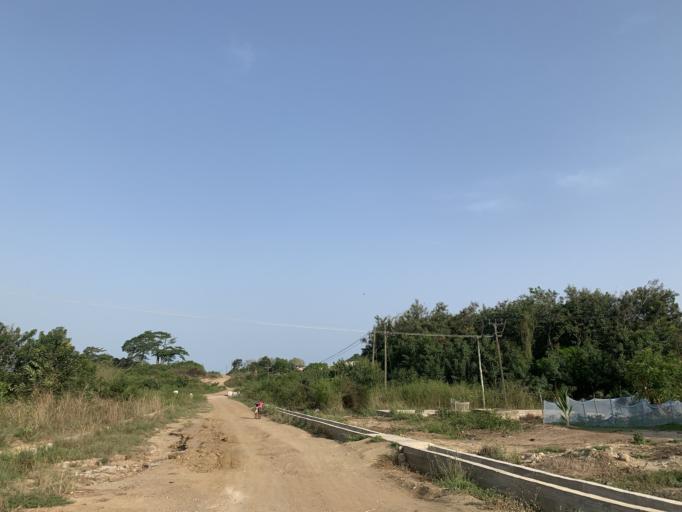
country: GH
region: Central
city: Winneba
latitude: 5.3801
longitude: -0.6190
